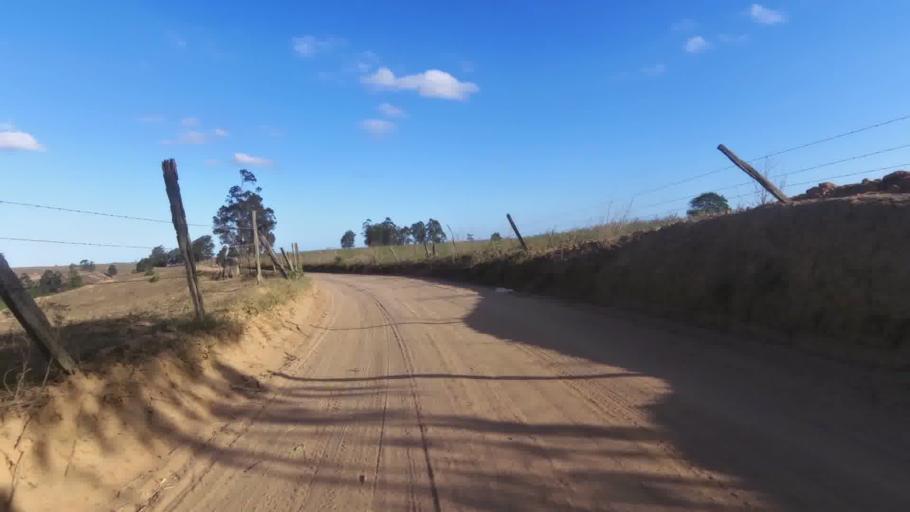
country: BR
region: Espirito Santo
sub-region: Marataizes
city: Marataizes
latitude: -21.1627
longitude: -41.0574
